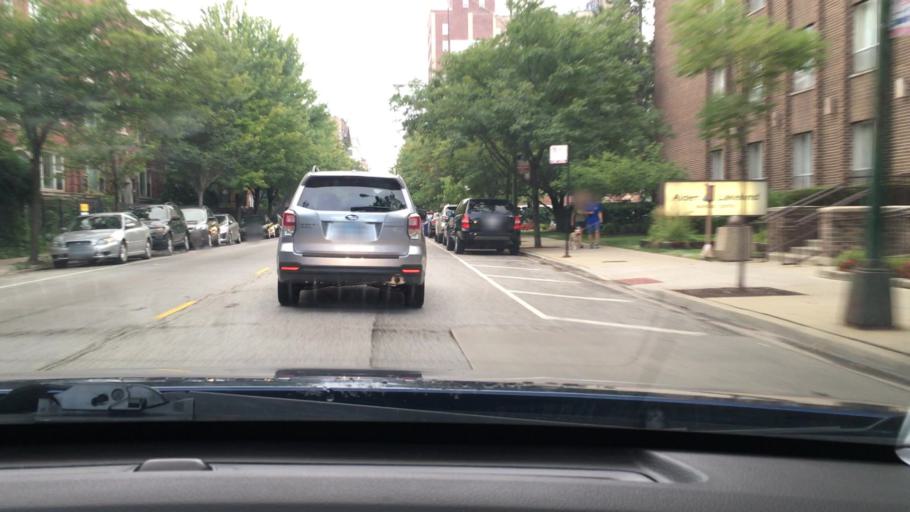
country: US
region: Illinois
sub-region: Cook County
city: Evanston
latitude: 41.9692
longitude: -87.6509
